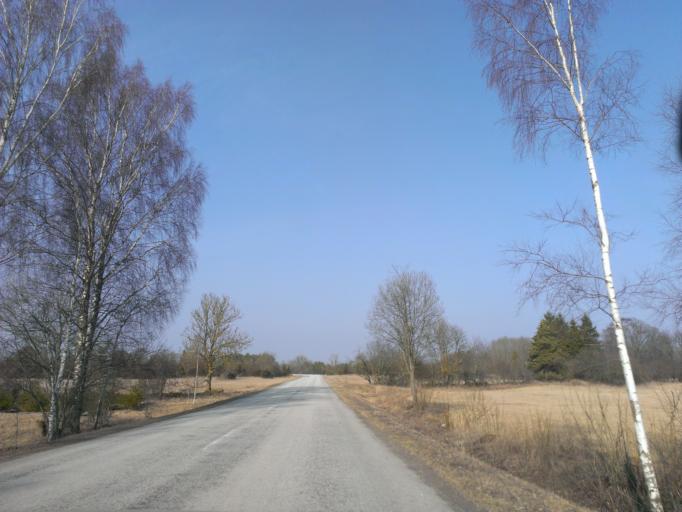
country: EE
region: Saare
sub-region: Orissaare vald
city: Orissaare
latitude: 58.5089
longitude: 23.1131
